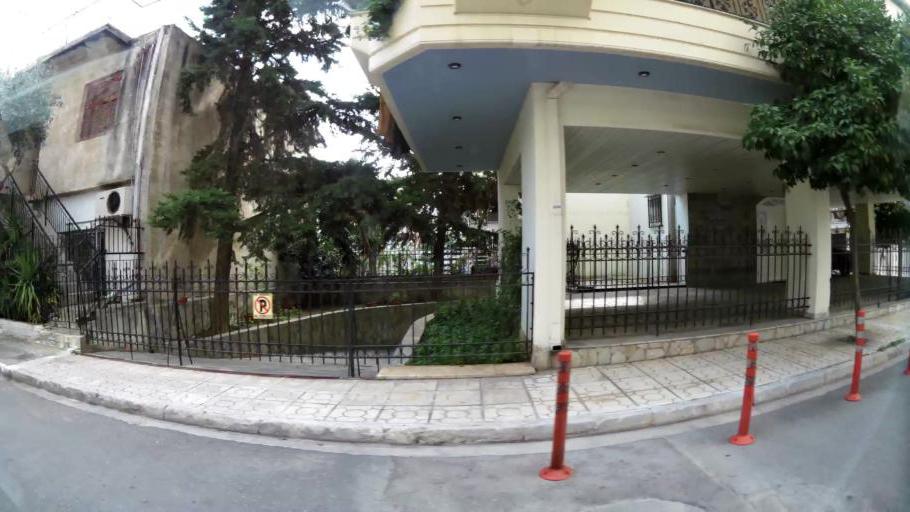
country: GR
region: Attica
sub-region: Nomarchia Athinas
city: Petroupolis
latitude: 38.0313
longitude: 23.6748
